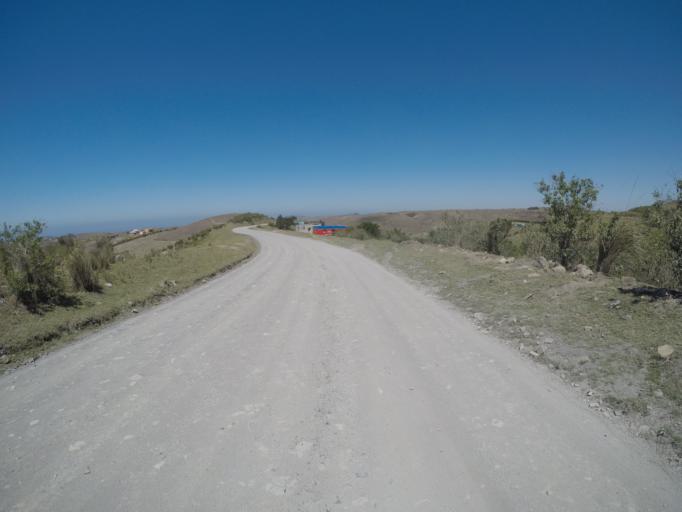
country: ZA
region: Eastern Cape
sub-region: OR Tambo District Municipality
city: Libode
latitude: -31.9888
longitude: 29.0535
